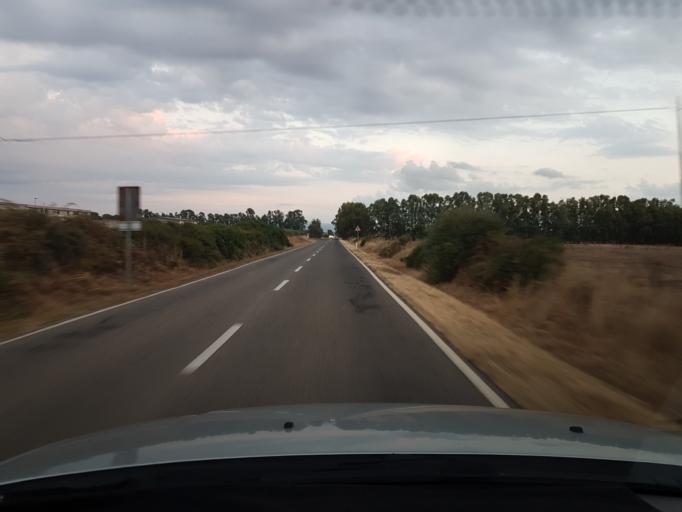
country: IT
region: Sardinia
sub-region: Provincia di Oristano
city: Milis
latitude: 40.0364
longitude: 8.6376
